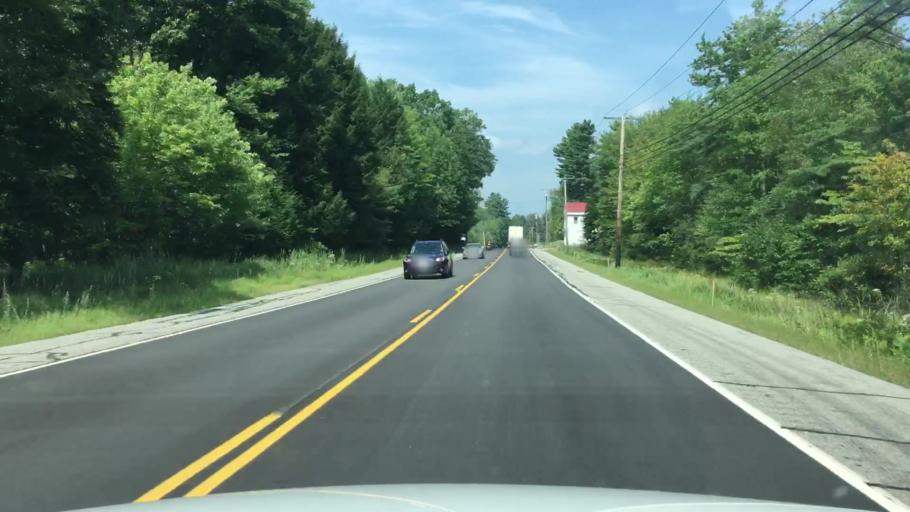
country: US
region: Maine
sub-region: Androscoggin County
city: Turner
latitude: 44.2372
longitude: -70.2577
